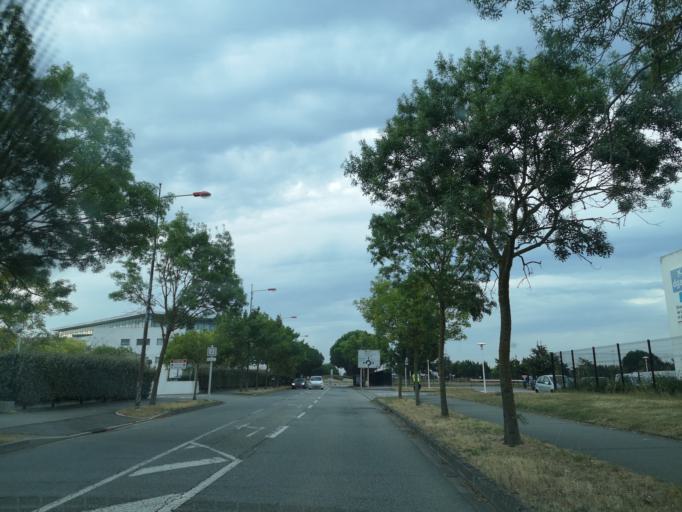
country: FR
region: Midi-Pyrenees
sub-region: Departement de la Haute-Garonne
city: Cugnaux
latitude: 43.5796
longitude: 1.3779
